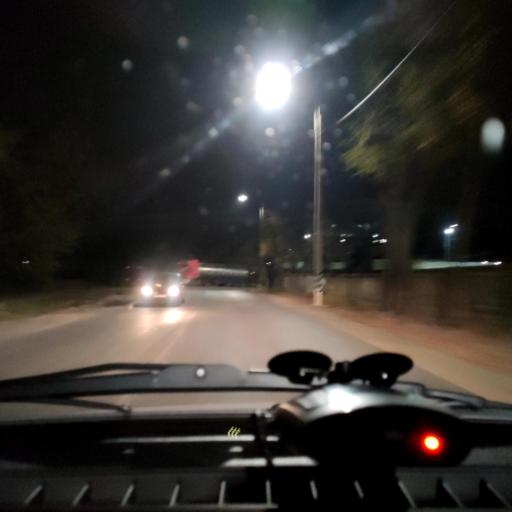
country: RU
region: Voronezj
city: Semiluki
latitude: 51.6797
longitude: 39.0287
